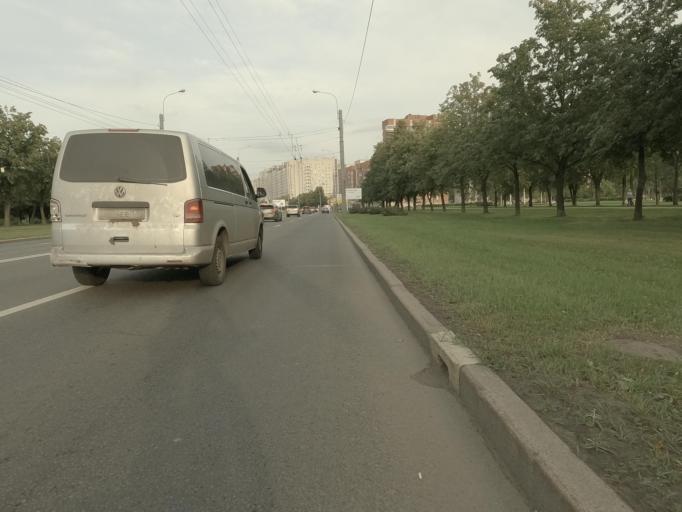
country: RU
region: St.-Petersburg
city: Uritsk
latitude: 59.8336
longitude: 30.1621
